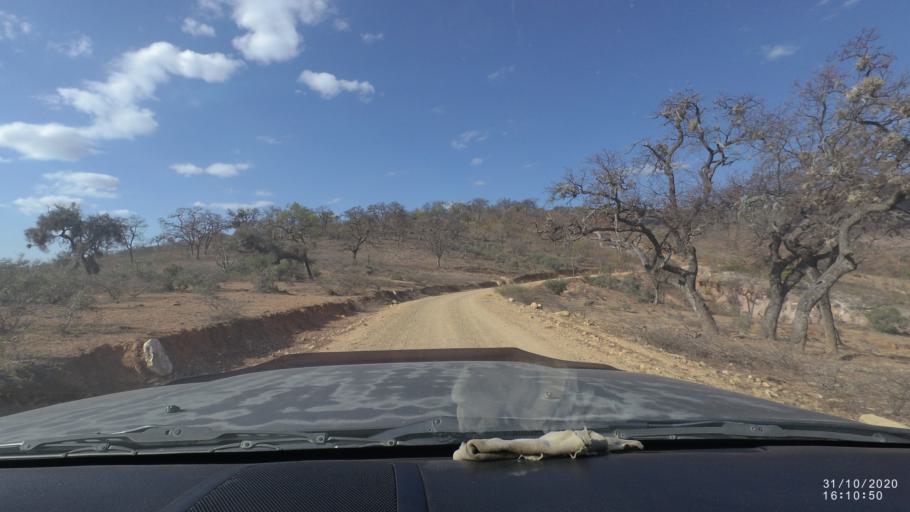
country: BO
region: Chuquisaca
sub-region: Provincia Zudanez
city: Mojocoya
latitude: -18.3820
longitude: -64.6271
